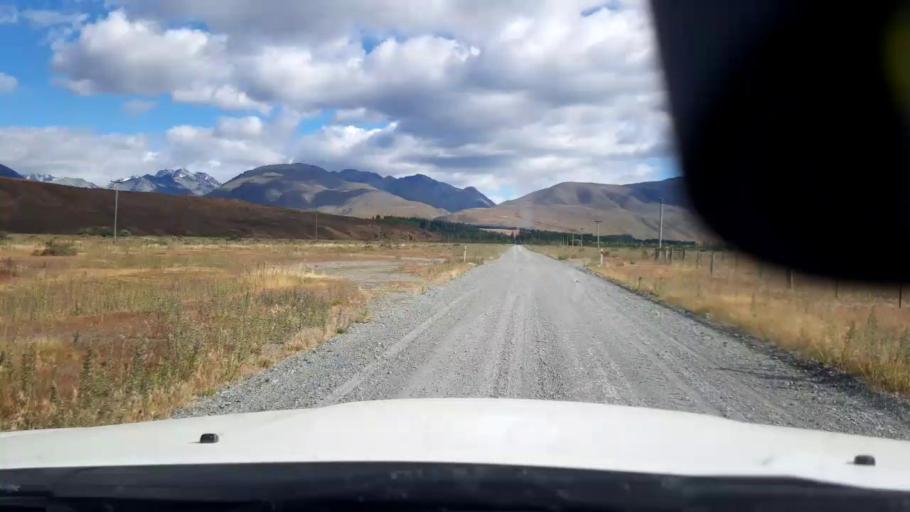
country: NZ
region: Canterbury
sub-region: Timaru District
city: Pleasant Point
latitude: -43.8873
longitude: 170.4670
